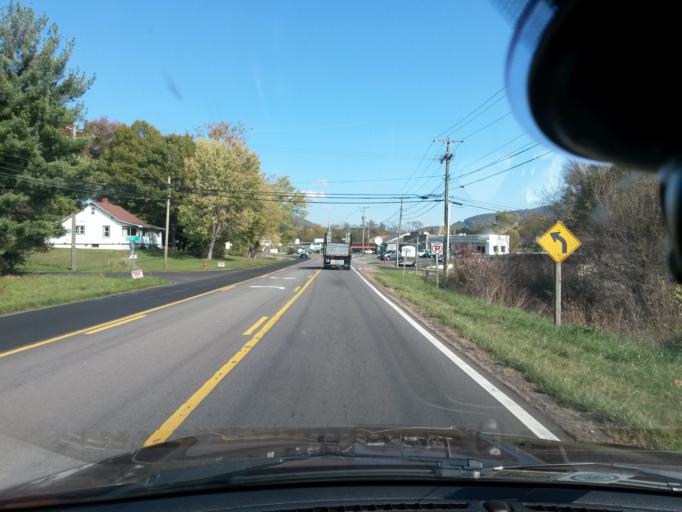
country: US
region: Virginia
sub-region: Botetourt County
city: Cloverdale
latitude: 37.3656
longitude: -79.9138
